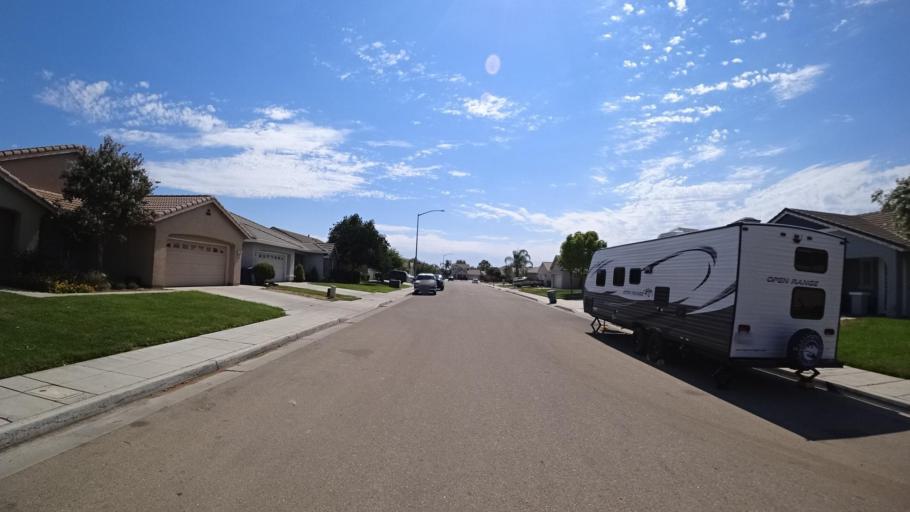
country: US
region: California
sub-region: Fresno County
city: Sunnyside
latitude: 36.7106
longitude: -119.7160
